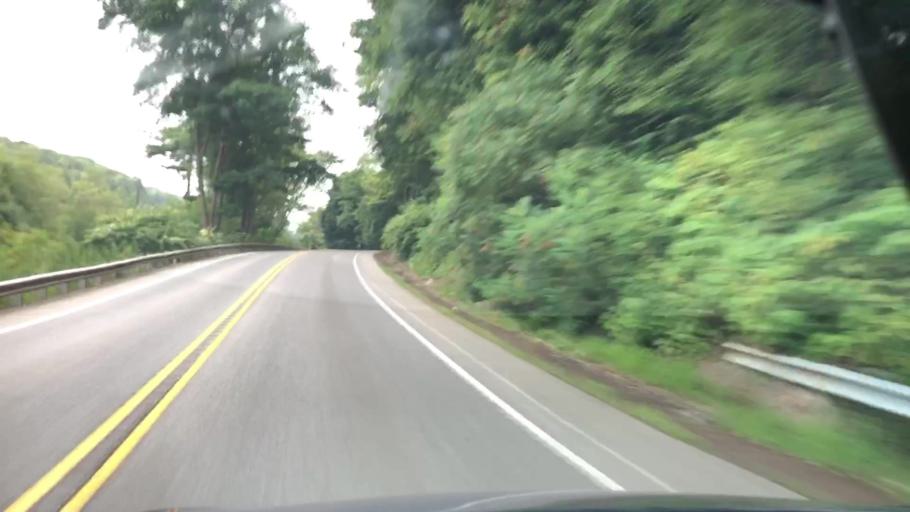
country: US
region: Pennsylvania
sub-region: Venango County
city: Hasson Heights
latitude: 41.4992
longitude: -79.7015
